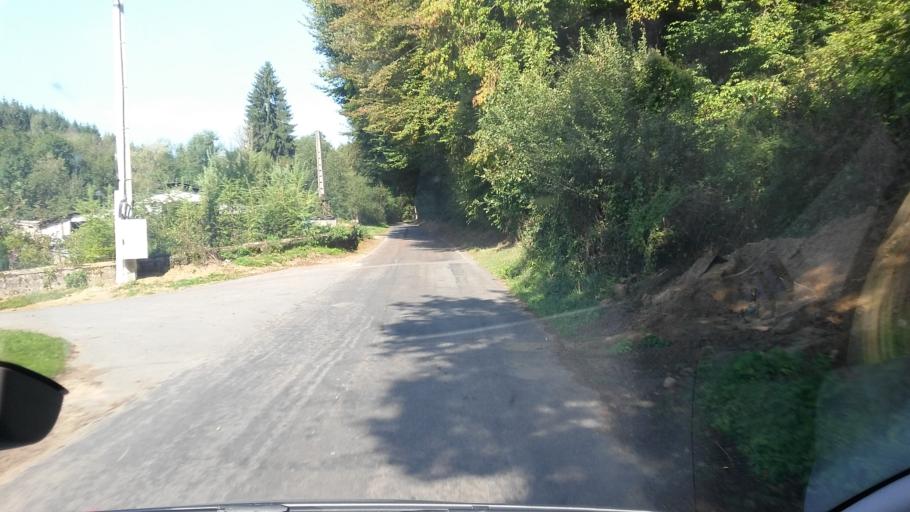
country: LU
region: Luxembourg
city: Eischen
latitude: 49.7013
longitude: 5.8565
